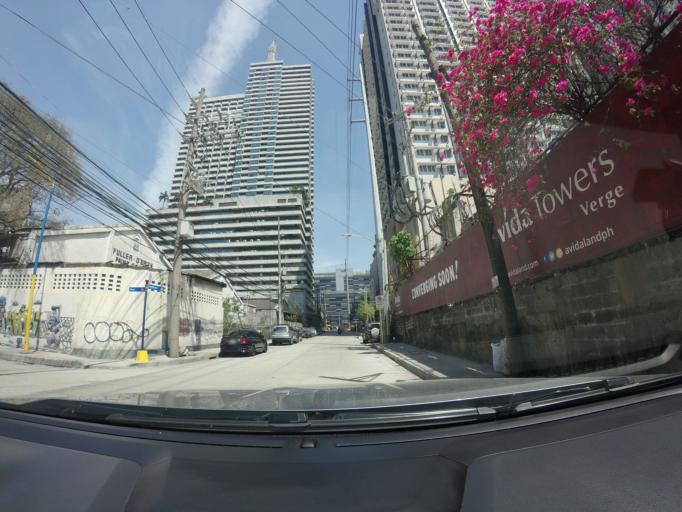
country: PH
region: Metro Manila
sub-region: Mandaluyong
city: Mandaluyong City
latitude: 14.5760
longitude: 121.0516
